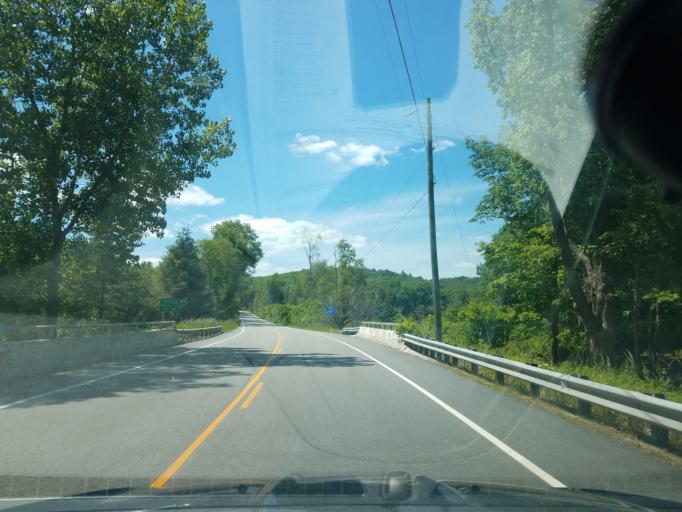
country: US
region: Connecticut
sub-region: Litchfield County
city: Winchester Center
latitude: 41.9139
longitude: -73.1850
